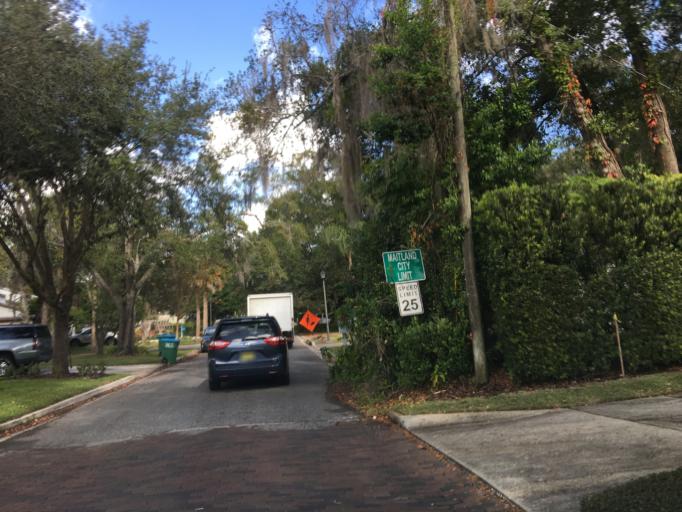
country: US
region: Florida
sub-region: Orange County
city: Maitland
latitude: 28.6118
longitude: -81.3633
